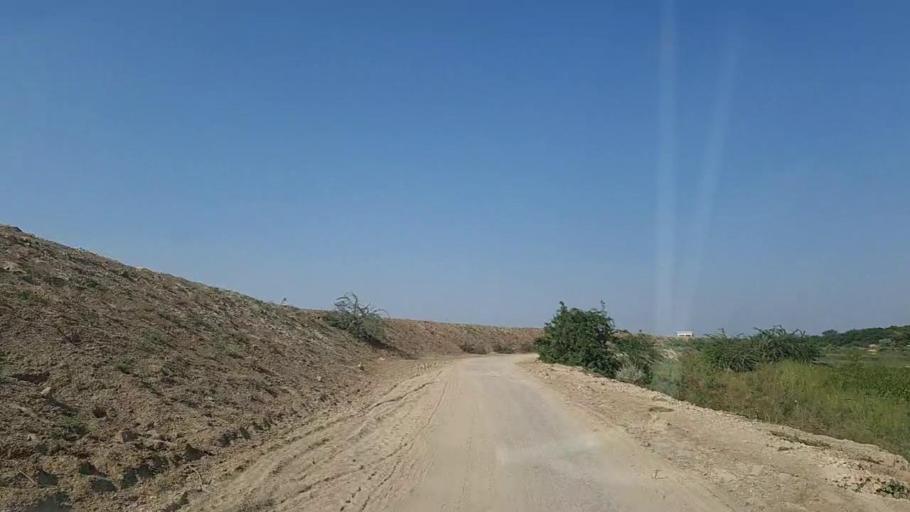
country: PK
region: Sindh
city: Chuhar Jamali
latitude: 24.5676
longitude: 68.0297
